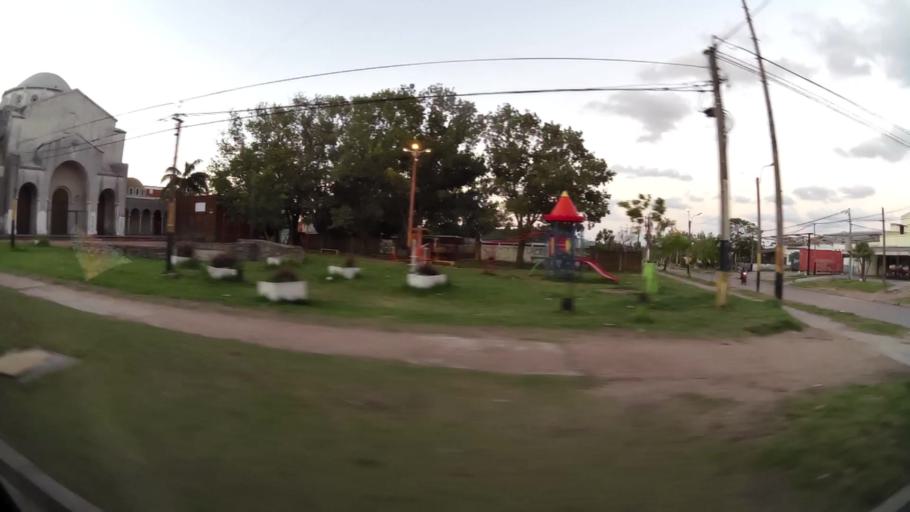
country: UY
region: Canelones
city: Paso de Carrasco
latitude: -34.8723
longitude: -56.0973
